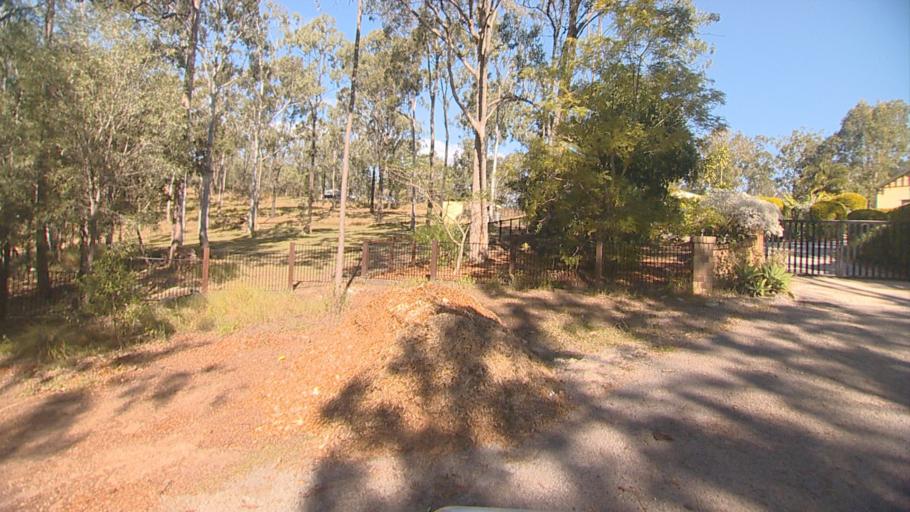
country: AU
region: Queensland
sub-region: Logan
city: Chambers Flat
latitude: -27.8207
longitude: 153.0766
